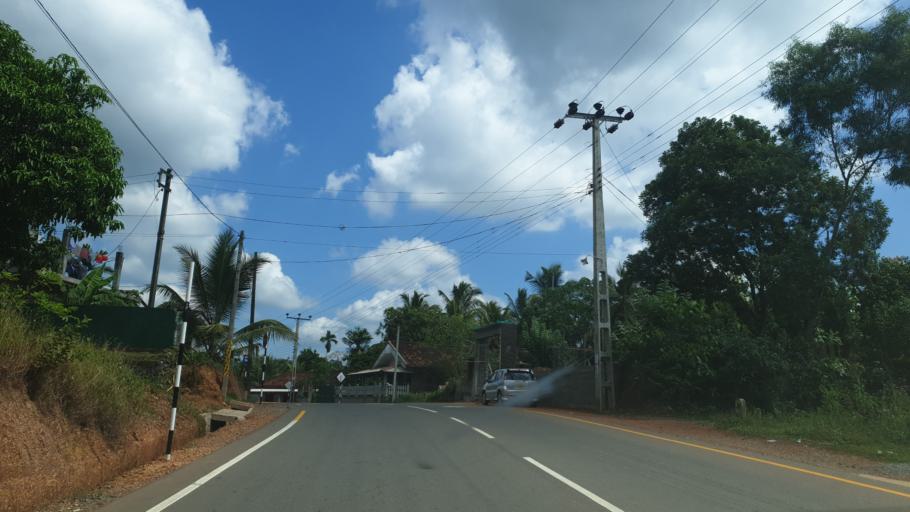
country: LK
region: Western
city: Panadura
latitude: 6.6655
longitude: 79.9596
